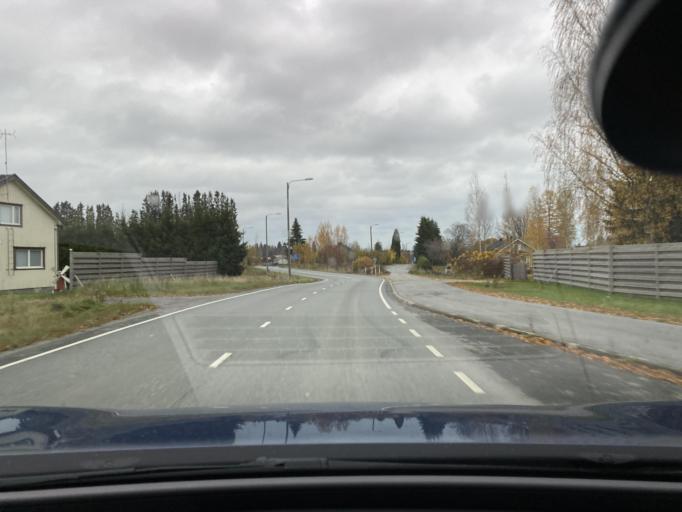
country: FI
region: Satakunta
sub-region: Pori
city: Huittinen
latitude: 61.1536
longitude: 22.6614
